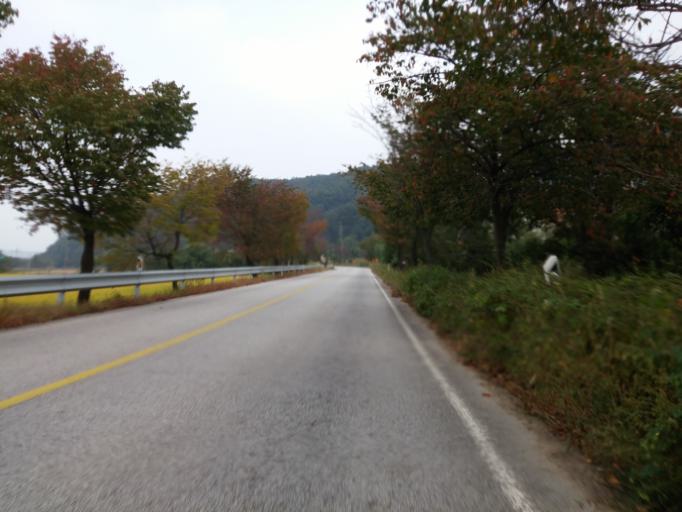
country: KR
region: Chungcheongbuk-do
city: Okcheon
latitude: 36.4158
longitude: 127.7713
